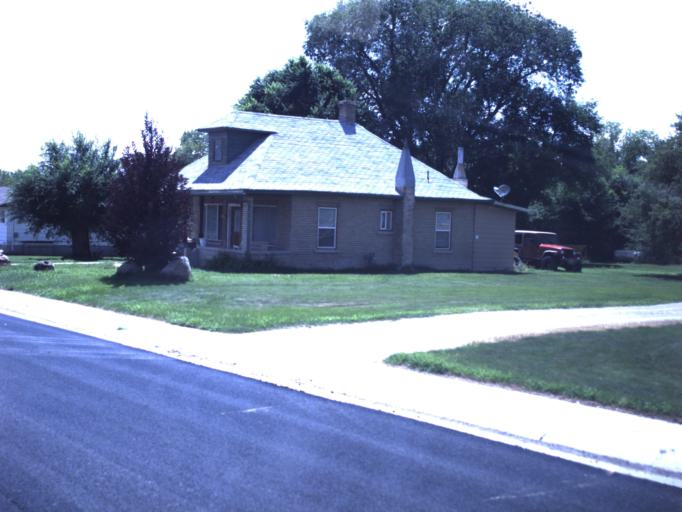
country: US
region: Utah
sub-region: Emery County
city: Orangeville
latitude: 39.2333
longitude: -111.0533
